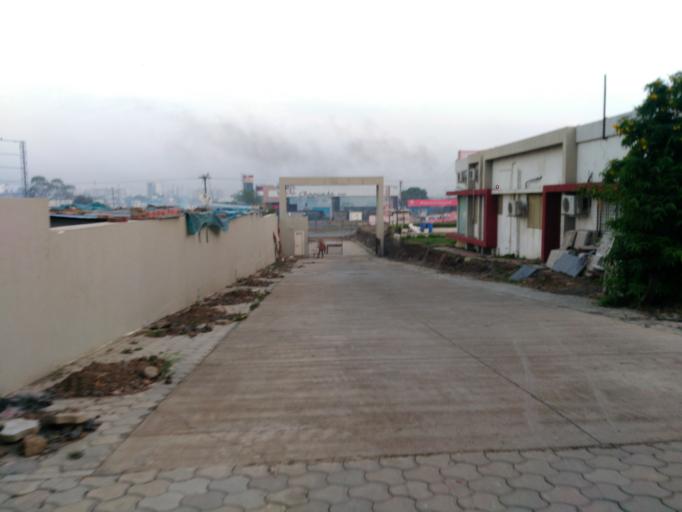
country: IN
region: Maharashtra
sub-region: Pune Division
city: Pune
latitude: 18.4502
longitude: 73.8974
